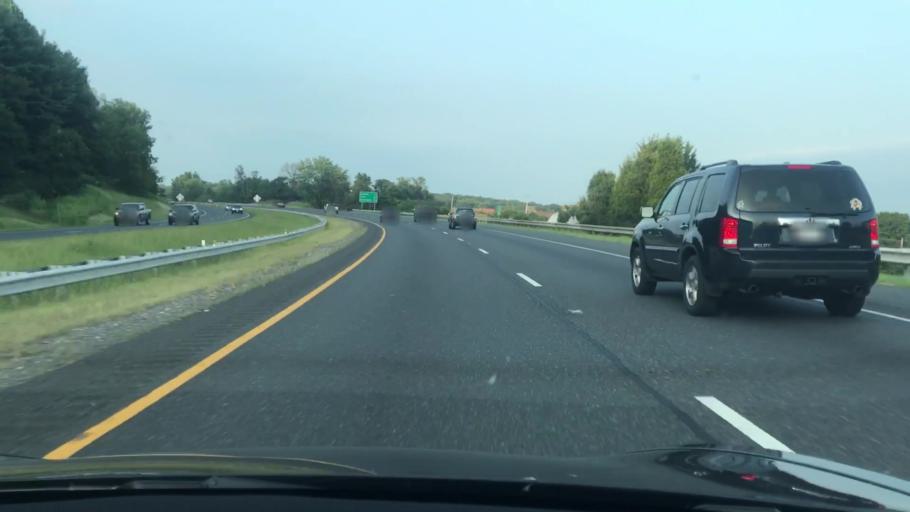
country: US
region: Maryland
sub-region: Baltimore County
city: Hunt Valley
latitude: 39.5969
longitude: -76.6647
